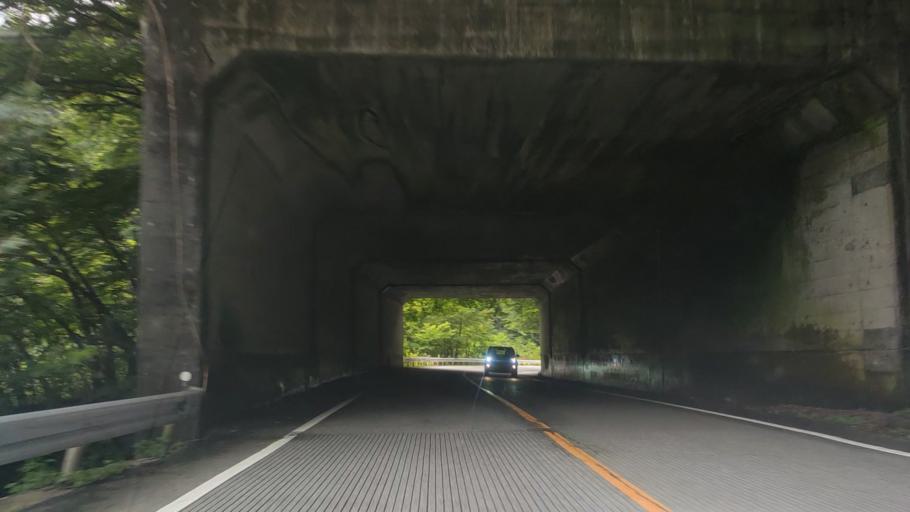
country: JP
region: Tochigi
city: Nikko
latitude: 36.7004
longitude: 139.5078
